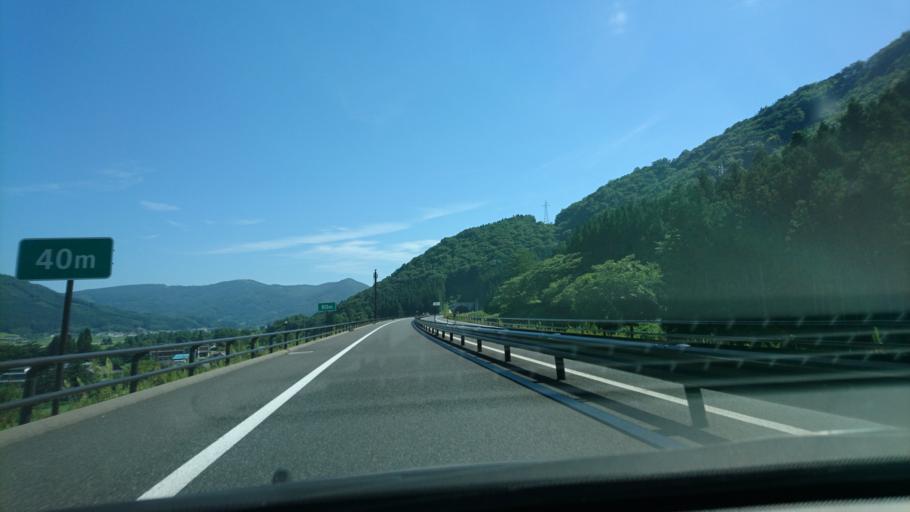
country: JP
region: Iwate
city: Tono
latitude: 39.3124
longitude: 141.4470
